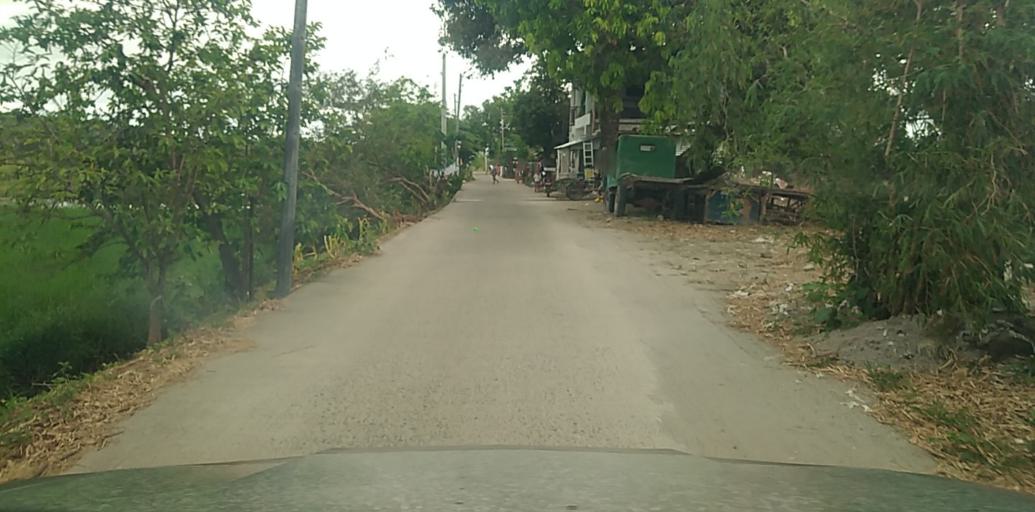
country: PH
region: Central Luzon
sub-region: Province of Pampanga
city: Panlinlang
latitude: 15.1806
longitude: 120.6996
